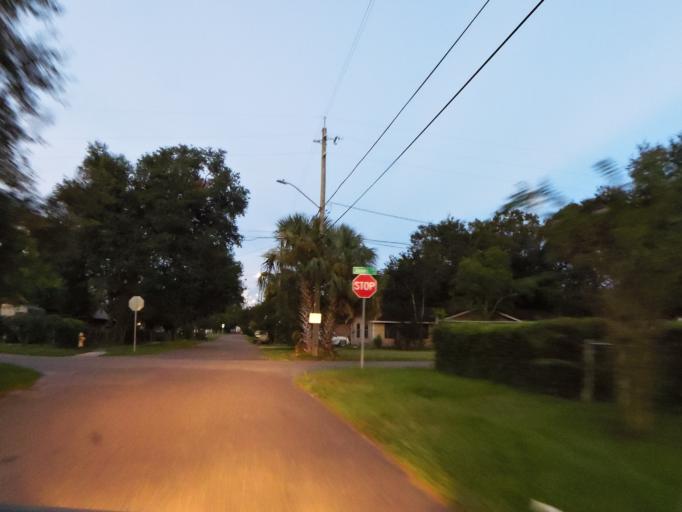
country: US
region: Florida
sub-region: Duval County
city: Jacksonville
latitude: 30.3568
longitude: -81.6344
